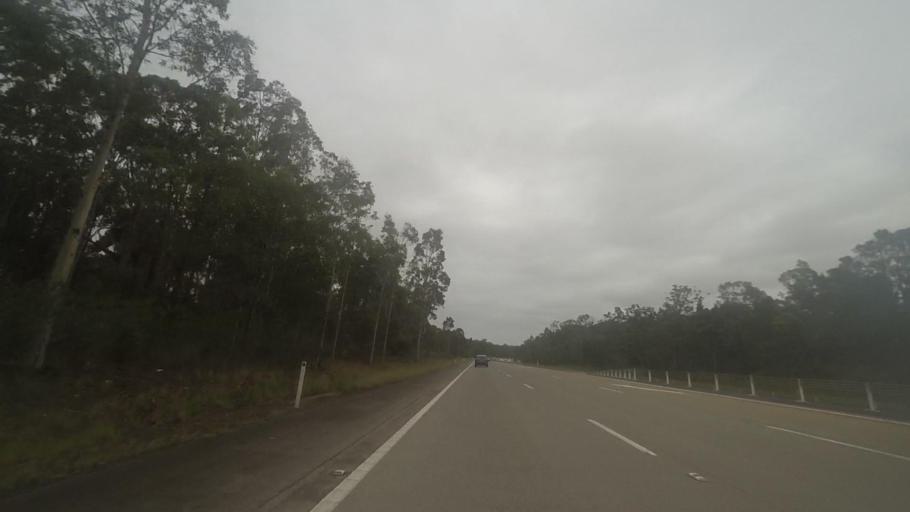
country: AU
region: New South Wales
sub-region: Port Stephens Shire
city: Medowie
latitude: -32.6900
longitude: 151.8092
